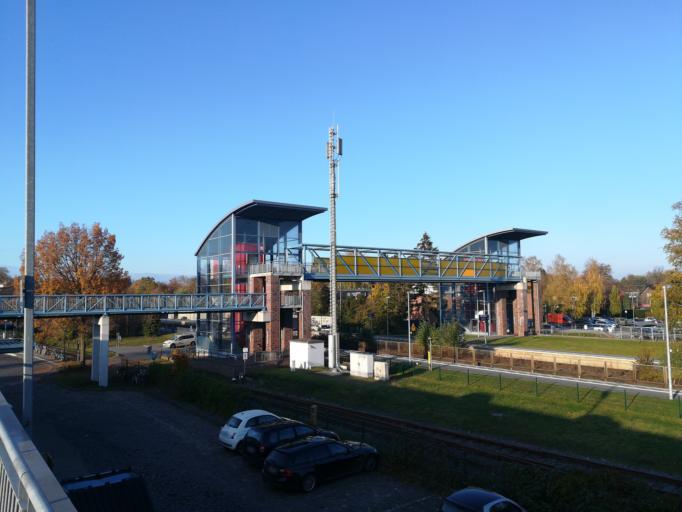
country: DE
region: Schleswig-Holstein
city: Tornesch
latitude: 53.6959
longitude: 9.7158
